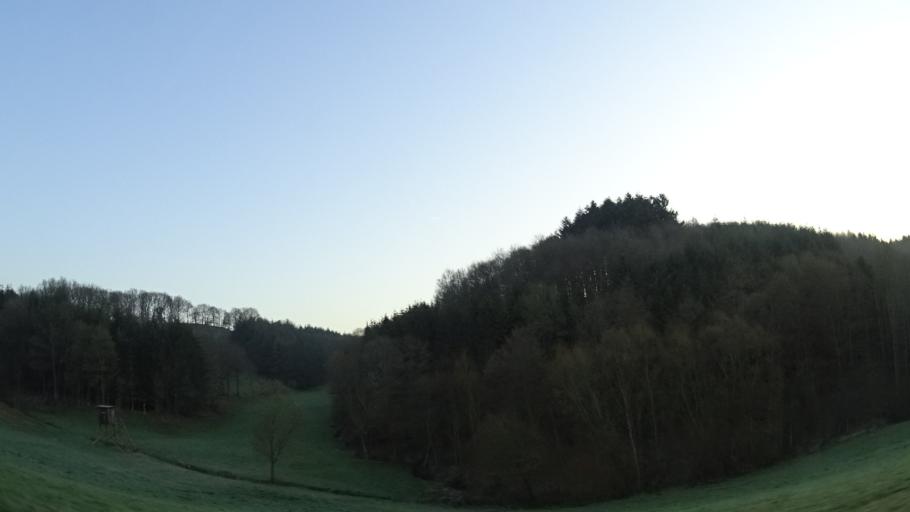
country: DE
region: Rheinland-Pfalz
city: Kirrweiler
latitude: 49.6289
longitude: 7.5002
